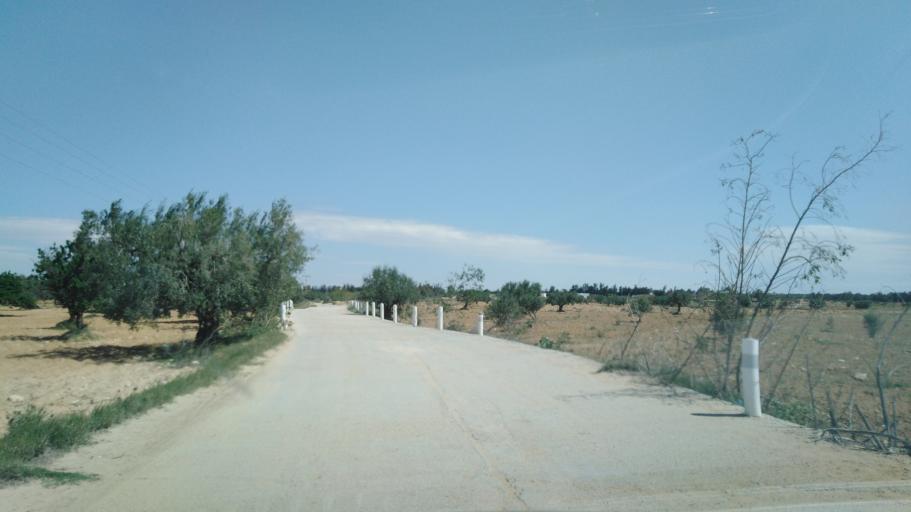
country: TN
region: Safaqis
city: Sfax
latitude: 34.7517
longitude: 10.5278
